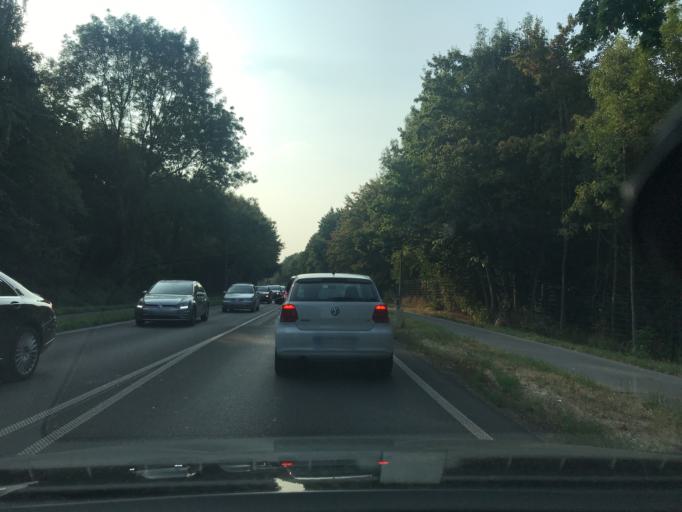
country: DE
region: North Rhine-Westphalia
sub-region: Regierungsbezirk Dusseldorf
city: Erkrath
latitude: 51.1961
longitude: 6.9074
